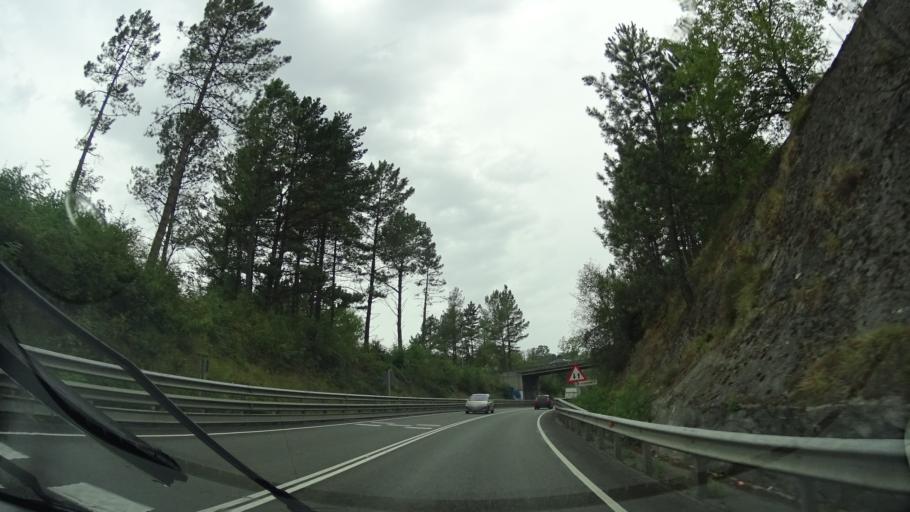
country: ES
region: Basque Country
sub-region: Bizkaia
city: Galdakao
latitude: 43.2224
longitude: -2.8187
